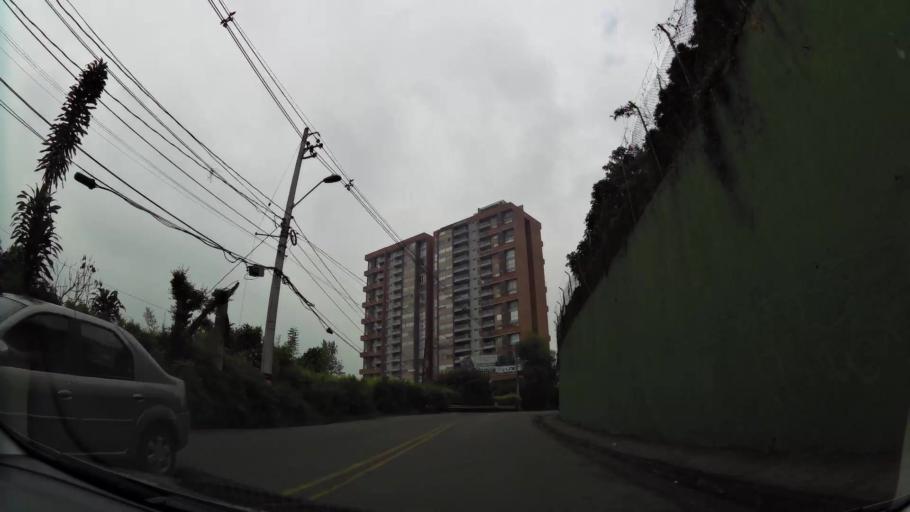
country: CO
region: Antioquia
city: Envigado
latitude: 6.1746
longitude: -75.5669
